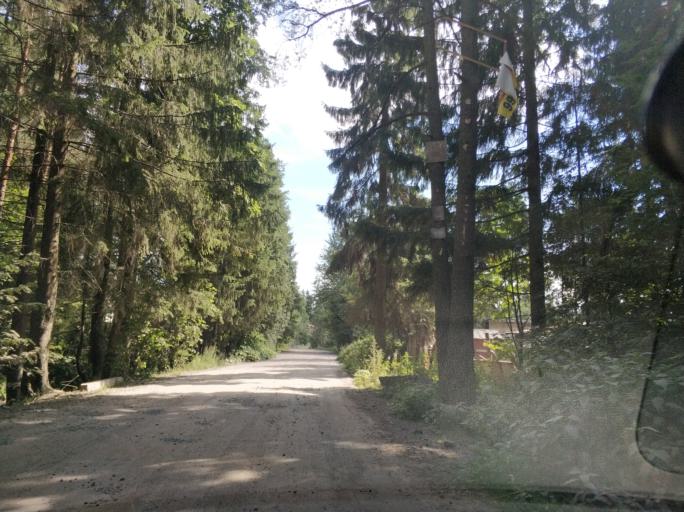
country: RU
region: Leningrad
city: Vsevolozhsk
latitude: 60.0212
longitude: 30.6127
